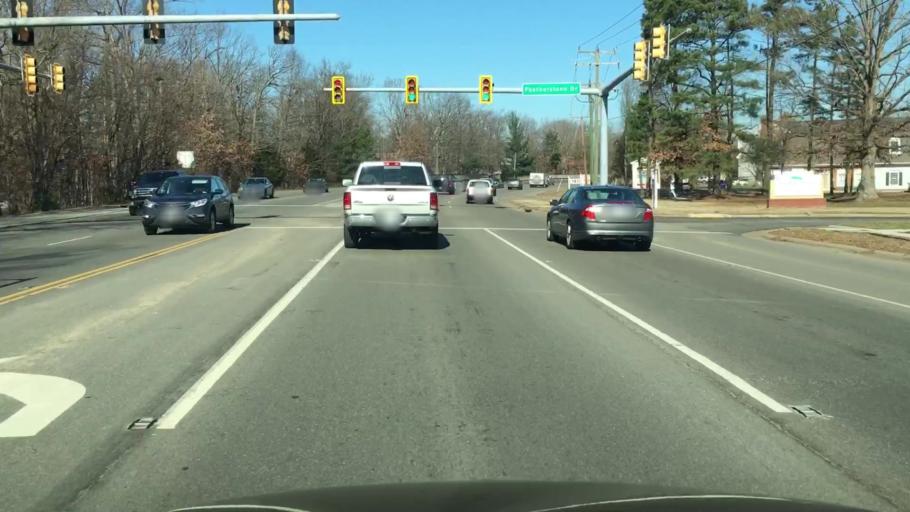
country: US
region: Virginia
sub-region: Chesterfield County
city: Bon Air
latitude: 37.5174
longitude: -77.6159
